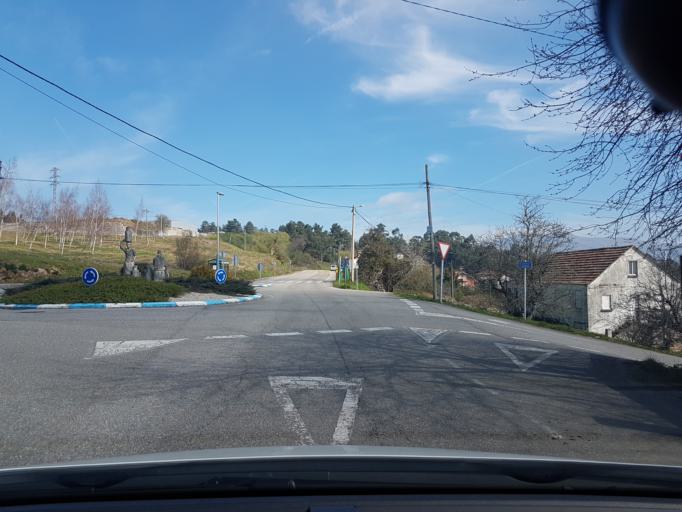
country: ES
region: Galicia
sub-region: Provincia de Pontevedra
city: Porrino
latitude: 42.2152
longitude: -8.6391
